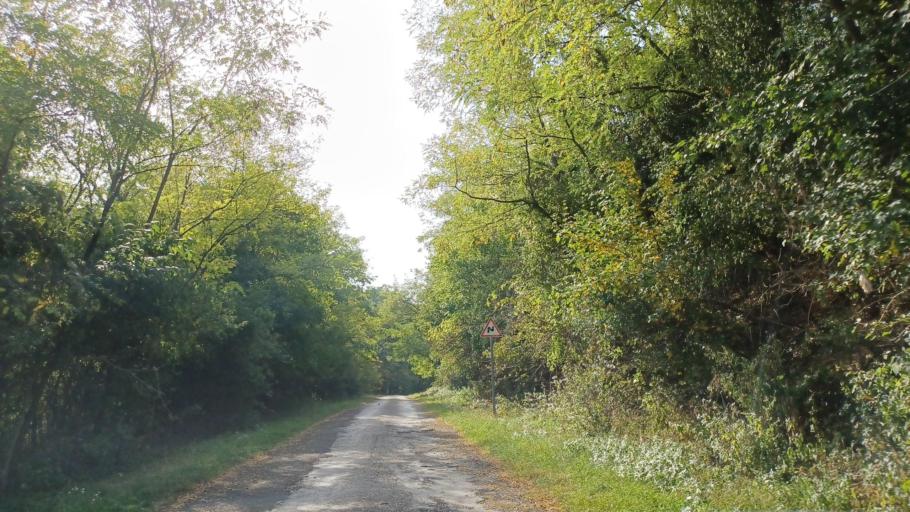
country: HU
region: Baranya
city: Mecseknadasd
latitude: 46.1915
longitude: 18.4493
